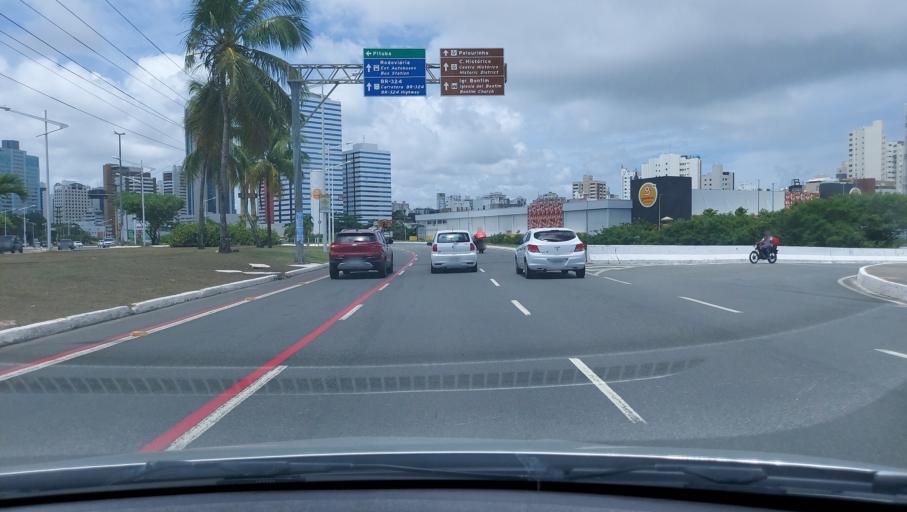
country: BR
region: Bahia
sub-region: Salvador
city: Salvador
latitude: -12.9929
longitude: -38.4501
